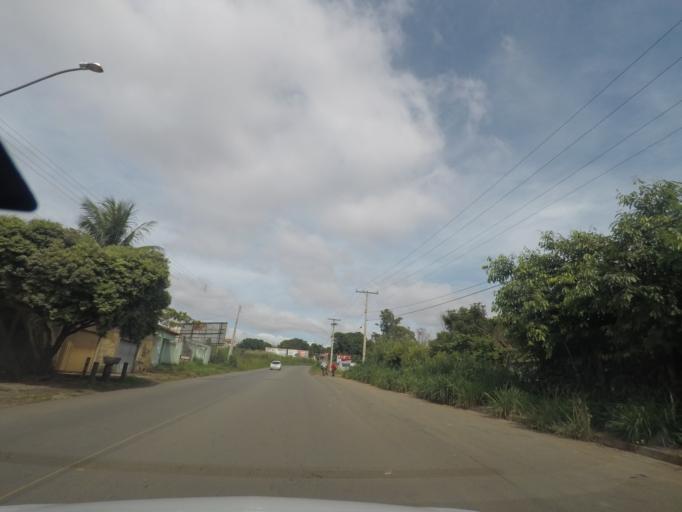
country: BR
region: Goias
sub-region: Goiania
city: Goiania
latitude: -16.6725
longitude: -49.2045
